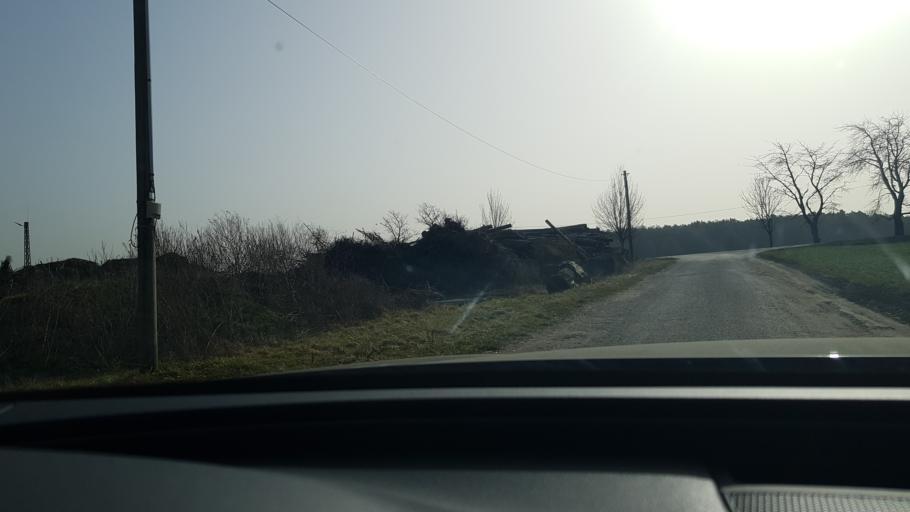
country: DE
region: Brandenburg
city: Schenkendobern
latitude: 51.9567
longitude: 14.6286
